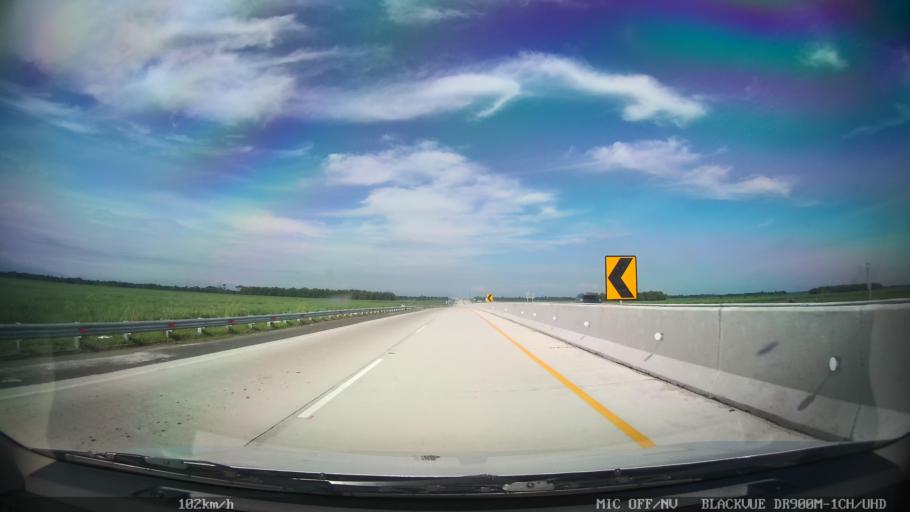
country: ID
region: North Sumatra
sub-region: Kabupaten Langkat
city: Stabat
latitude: 3.7133
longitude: 98.5234
